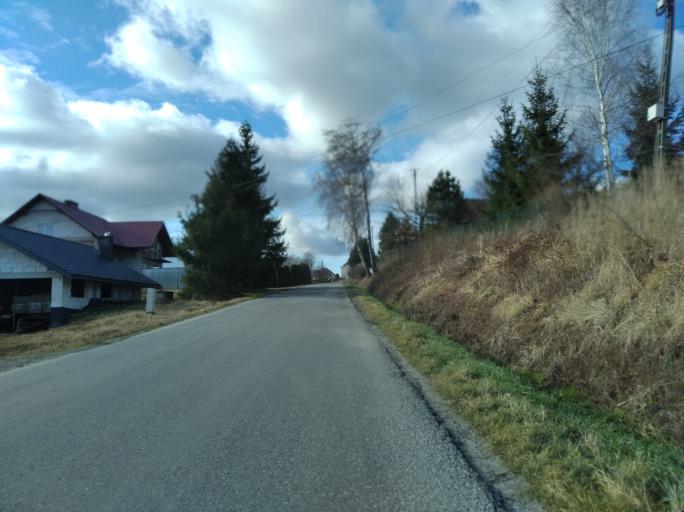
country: PL
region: Subcarpathian Voivodeship
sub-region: Powiat strzyzowski
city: Wisniowa
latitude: 49.9140
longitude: 21.7065
